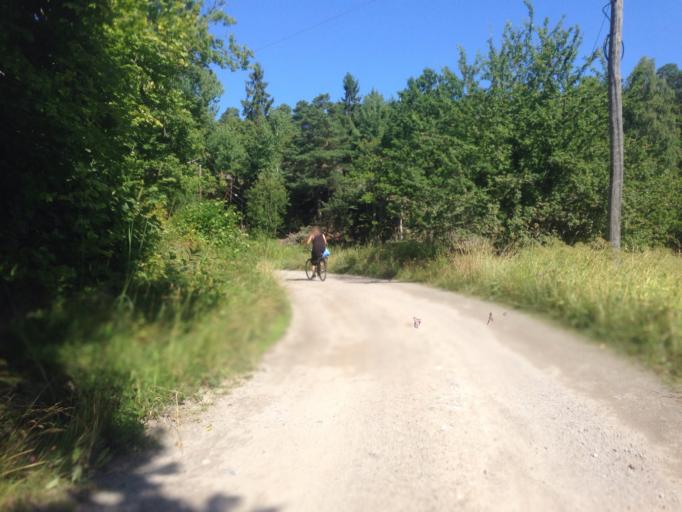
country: SE
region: Stockholm
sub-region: Vaxholms Kommun
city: Vaxholm
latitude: 59.3758
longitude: 18.3905
